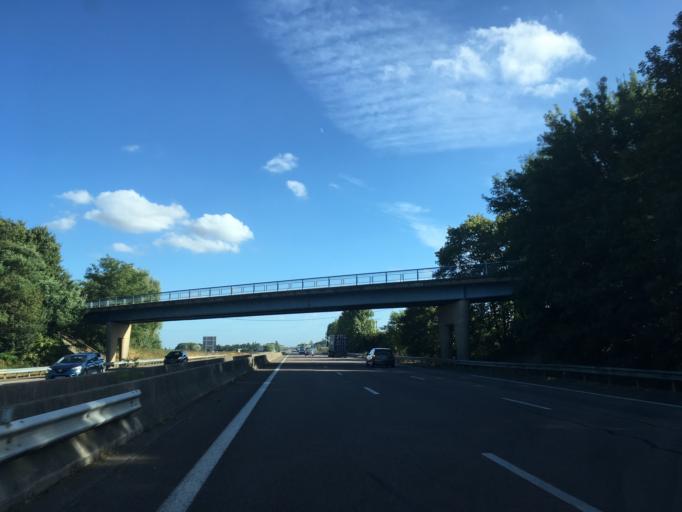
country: FR
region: Haute-Normandie
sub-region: Departement de l'Eure
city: Saint-Pierre-du-Vauvray
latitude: 49.2203
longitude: 1.2130
